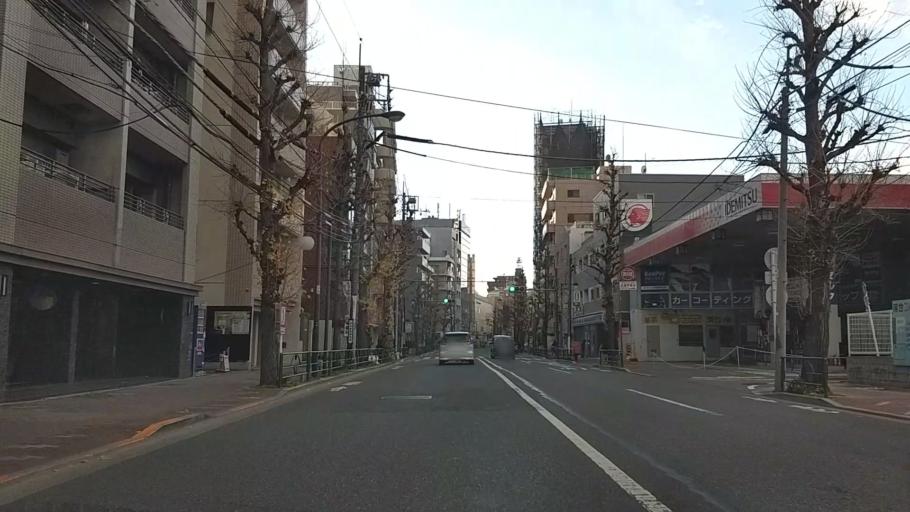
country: JP
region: Tokyo
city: Tokyo
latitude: 35.7221
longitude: 139.6991
